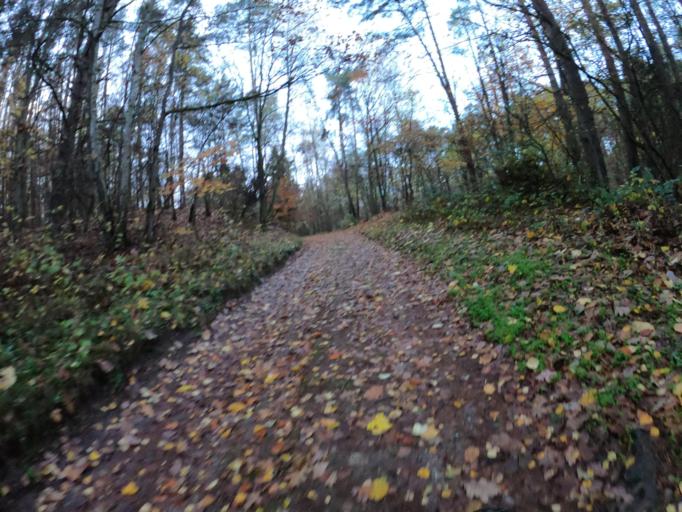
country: PL
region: West Pomeranian Voivodeship
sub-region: Powiat walecki
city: Tuczno
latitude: 53.1853
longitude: 16.1663
